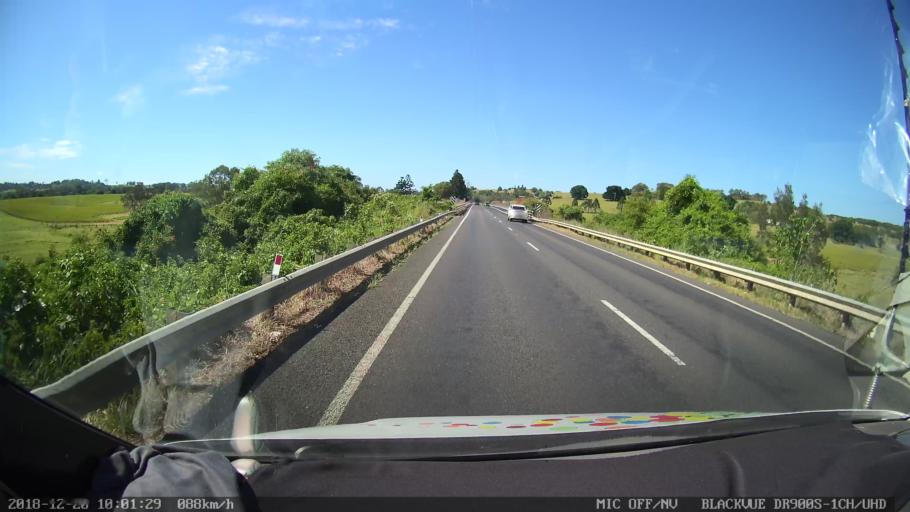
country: AU
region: New South Wales
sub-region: Lismore Municipality
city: Lismore
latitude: -28.8451
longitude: 153.2623
